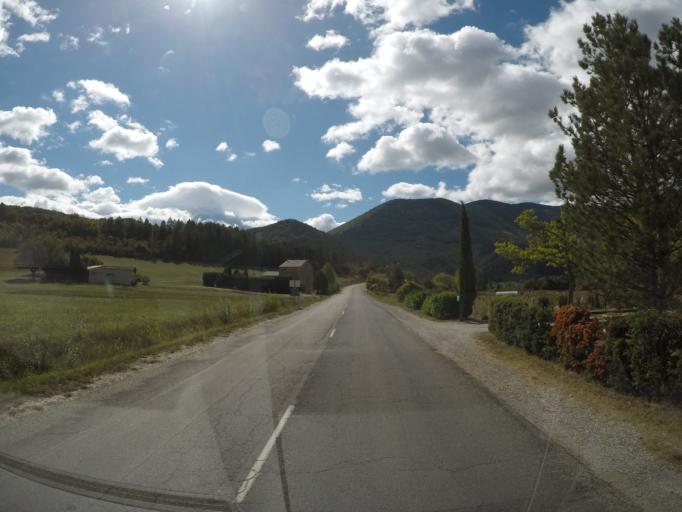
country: FR
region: Provence-Alpes-Cote d'Azur
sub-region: Departement du Vaucluse
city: Sault
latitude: 44.1715
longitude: 5.4352
